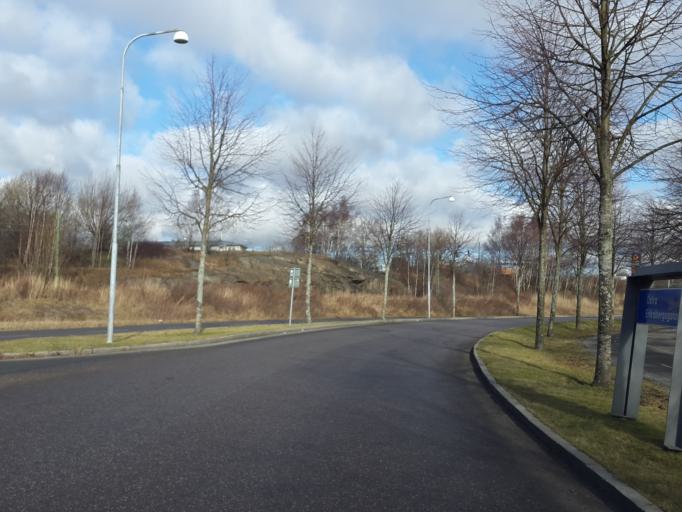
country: SE
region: Vaestra Goetaland
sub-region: Goteborg
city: Majorna
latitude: 57.7052
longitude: 11.9180
